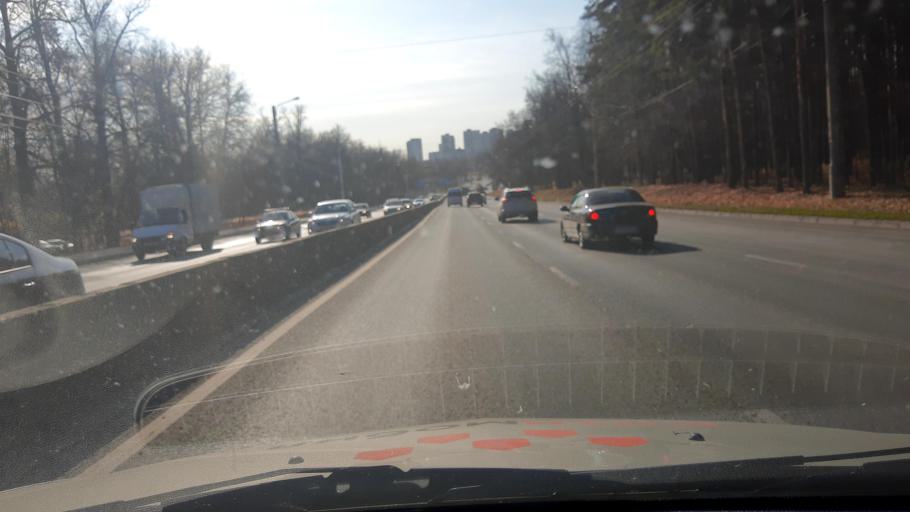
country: RU
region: Bashkortostan
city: Ufa
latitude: 54.7362
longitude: 56.0266
